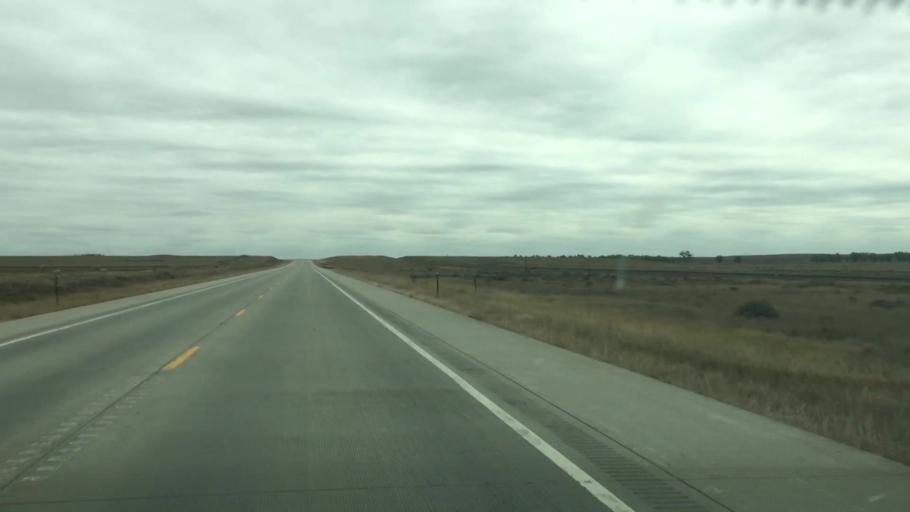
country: US
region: Colorado
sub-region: Kiowa County
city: Eads
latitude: 38.7688
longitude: -102.8591
